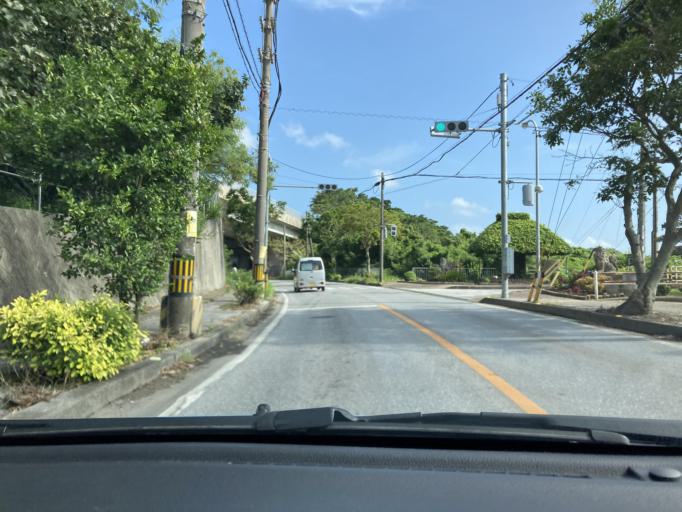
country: JP
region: Okinawa
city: Ginowan
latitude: 26.2791
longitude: 127.7841
